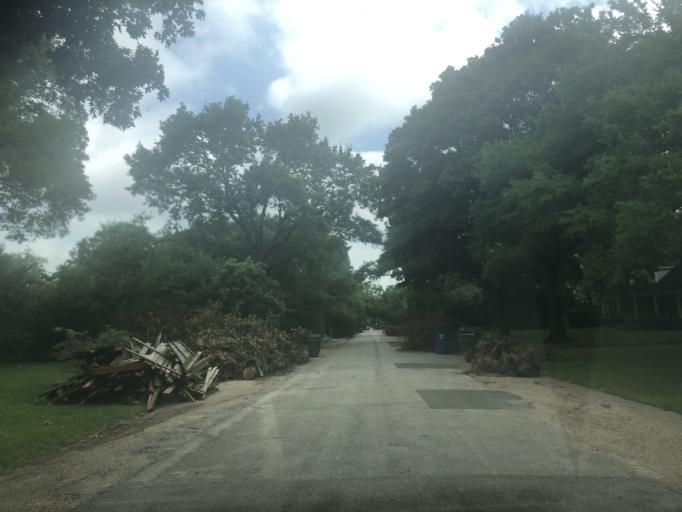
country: US
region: Texas
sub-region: Dallas County
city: University Park
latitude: 32.8582
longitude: -96.8319
